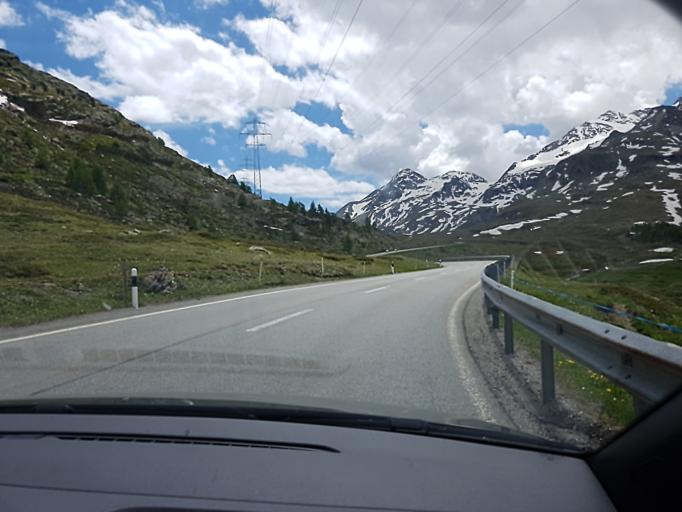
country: CH
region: Grisons
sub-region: Maloja District
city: Pontresina
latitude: 46.4326
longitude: 9.9979
